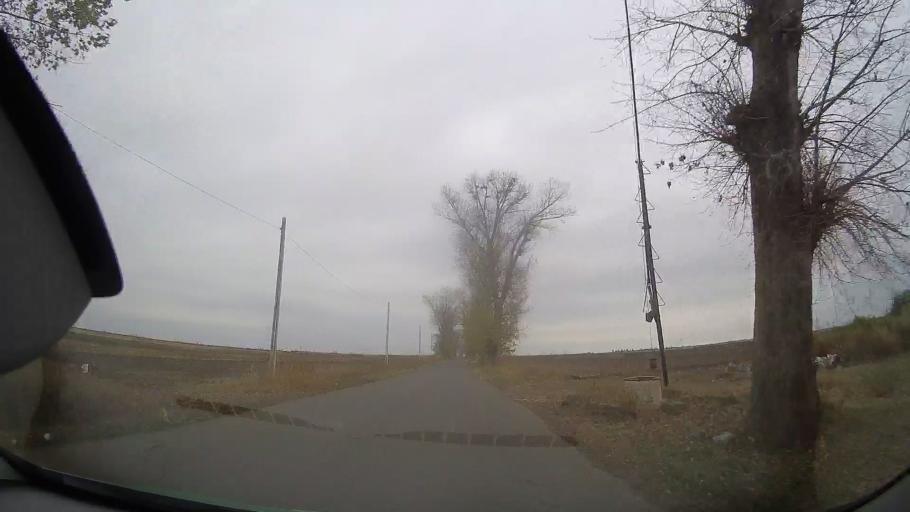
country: RO
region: Braila
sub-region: Comuna Ciocile
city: Ciocile
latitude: 44.8139
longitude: 27.2868
